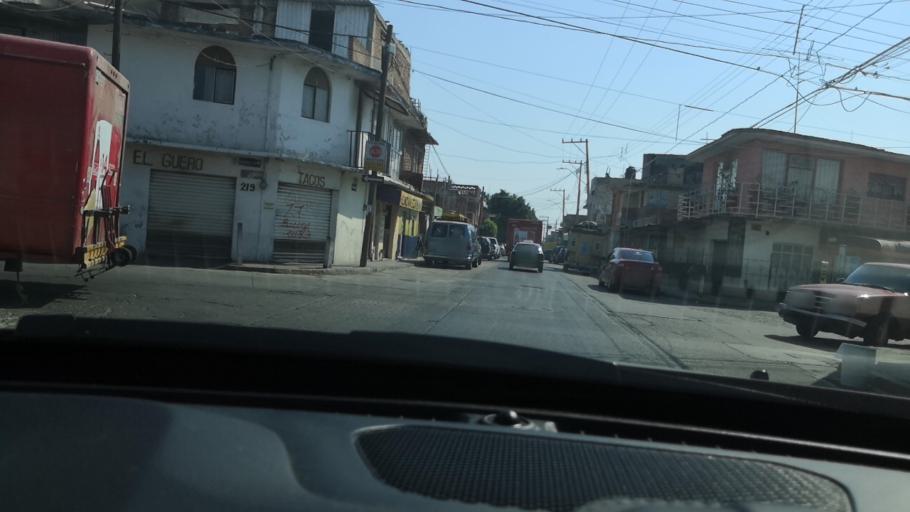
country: MX
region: Guanajuato
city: Leon
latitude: 21.1124
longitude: -101.6986
